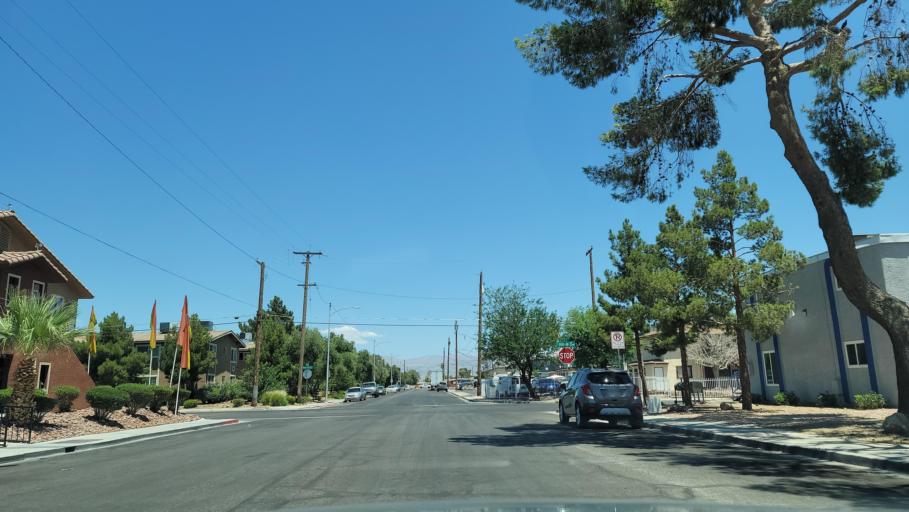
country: US
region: Nevada
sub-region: Clark County
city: North Las Vegas
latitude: 36.1863
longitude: -115.1183
